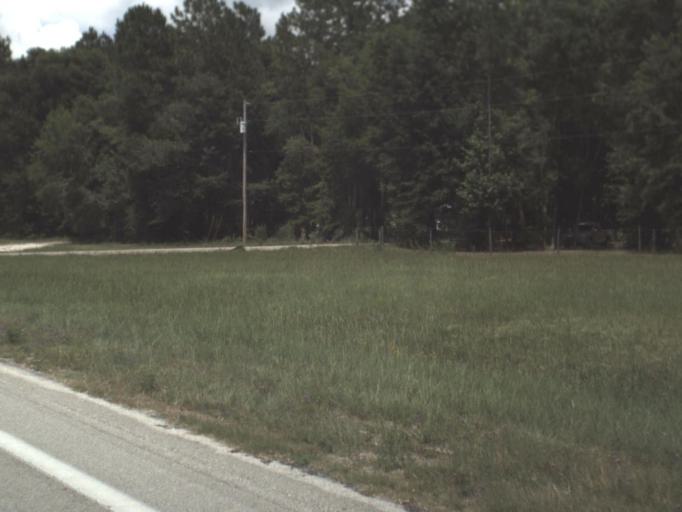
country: US
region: Florida
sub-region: Alachua County
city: Newberry
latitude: 29.6790
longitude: -82.6070
